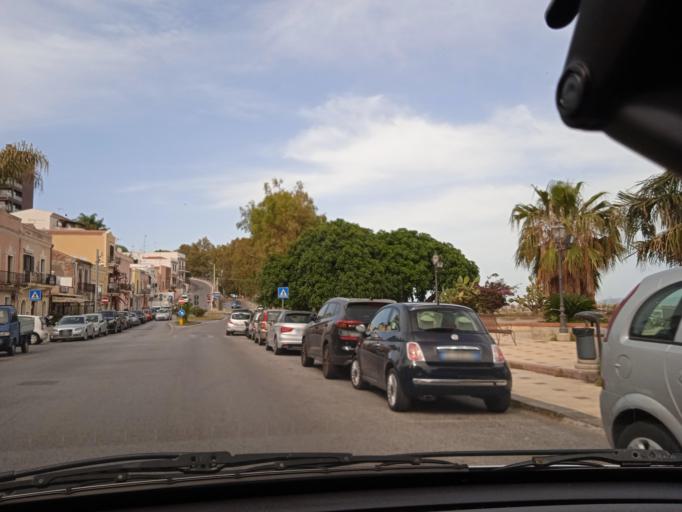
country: IT
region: Sicily
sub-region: Messina
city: Milazzo
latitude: 38.2296
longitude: 15.2468
